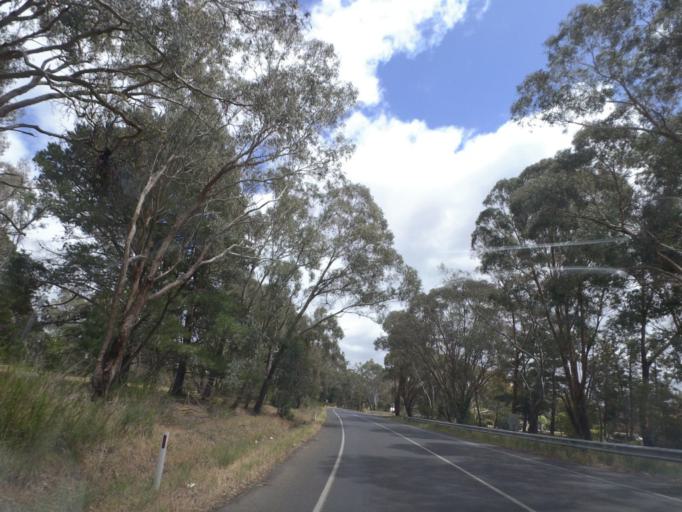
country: AU
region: Victoria
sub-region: Whittlesea
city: Whittlesea
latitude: -37.2139
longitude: 145.0506
